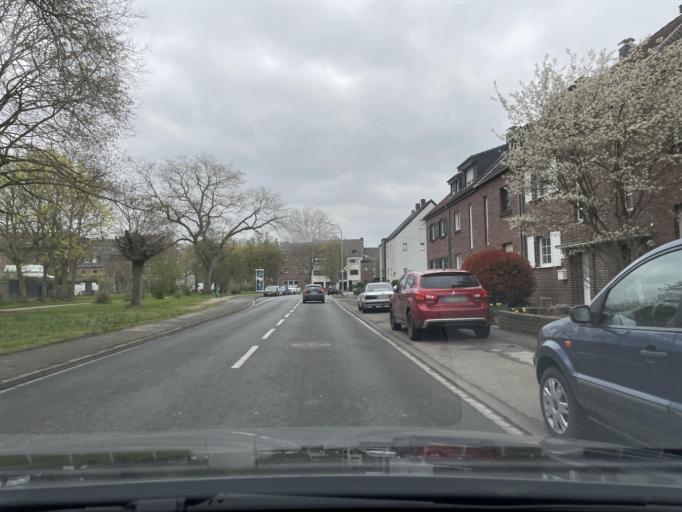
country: DE
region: North Rhine-Westphalia
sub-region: Regierungsbezirk Dusseldorf
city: Monchengladbach
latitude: 51.1594
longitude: 6.4560
